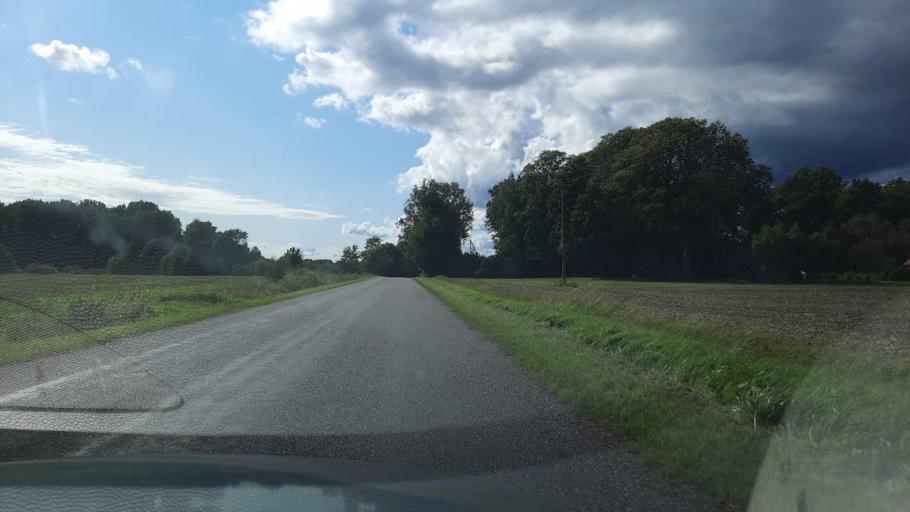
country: EE
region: Paernumaa
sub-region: Tootsi vald
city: Tootsi
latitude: 58.4831
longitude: 24.9080
